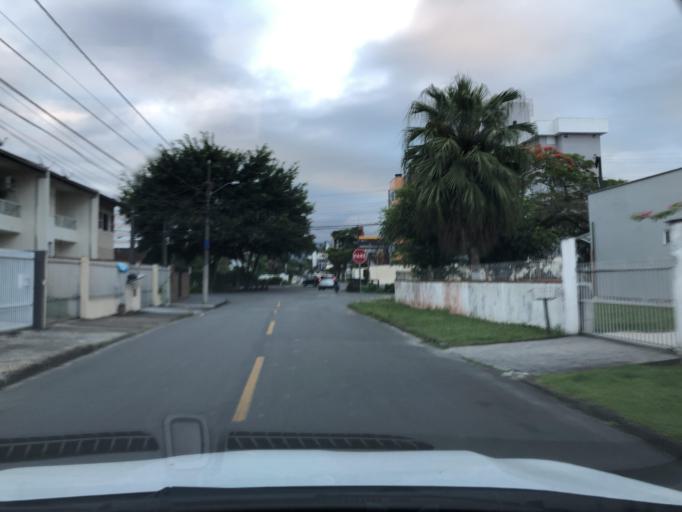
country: BR
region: Santa Catarina
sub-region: Joinville
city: Joinville
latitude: -26.2714
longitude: -48.8689
